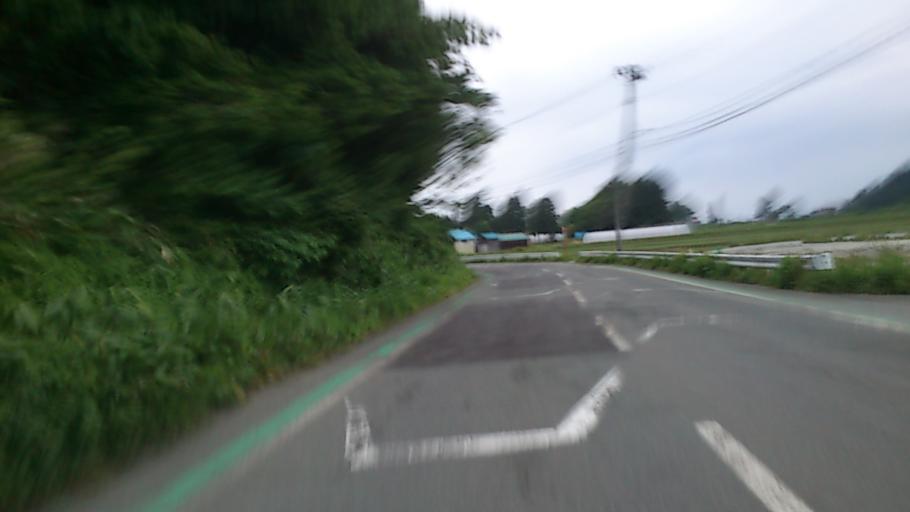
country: JP
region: Yamagata
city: Obanazawa
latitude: 38.5754
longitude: 140.4963
